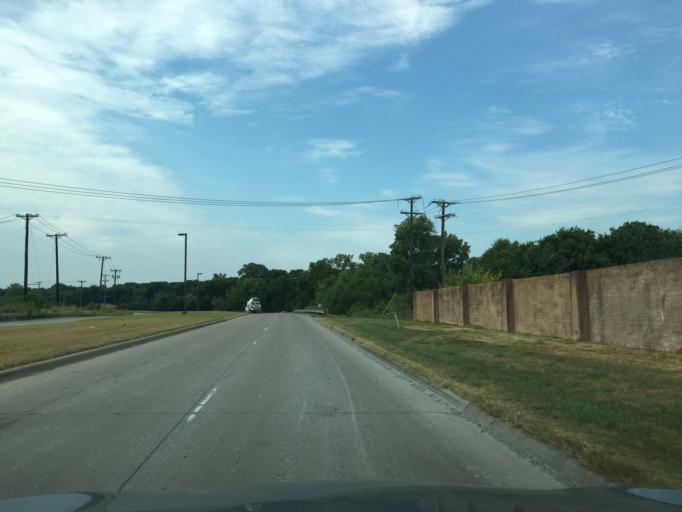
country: US
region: Texas
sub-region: Collin County
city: McKinney
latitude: 33.2029
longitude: -96.5995
